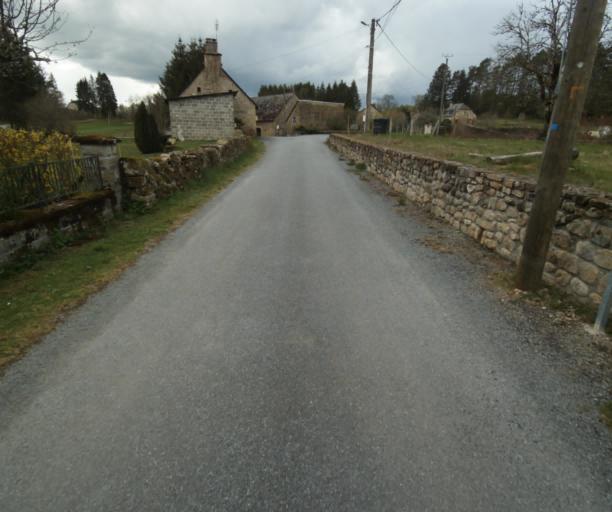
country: FR
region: Limousin
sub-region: Departement de la Correze
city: Correze
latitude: 45.2699
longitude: 1.9603
